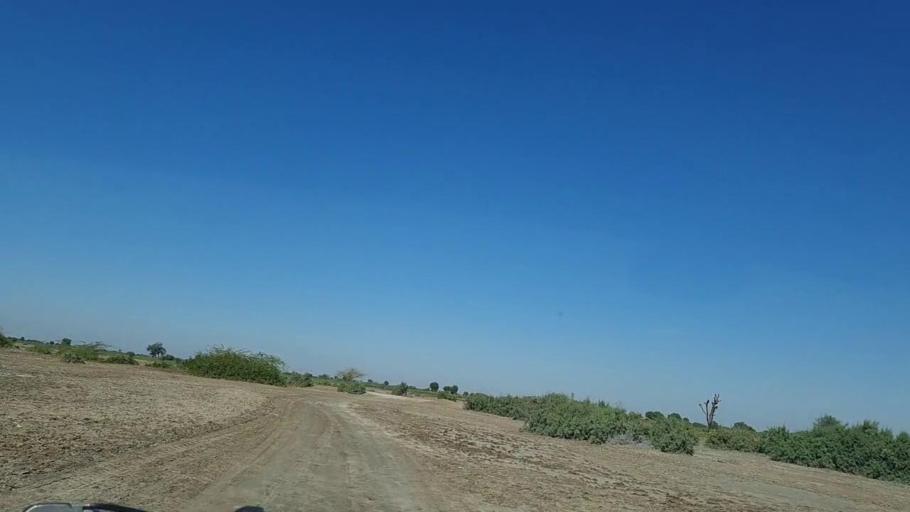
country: PK
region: Sindh
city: Pithoro
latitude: 25.5570
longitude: 69.4605
